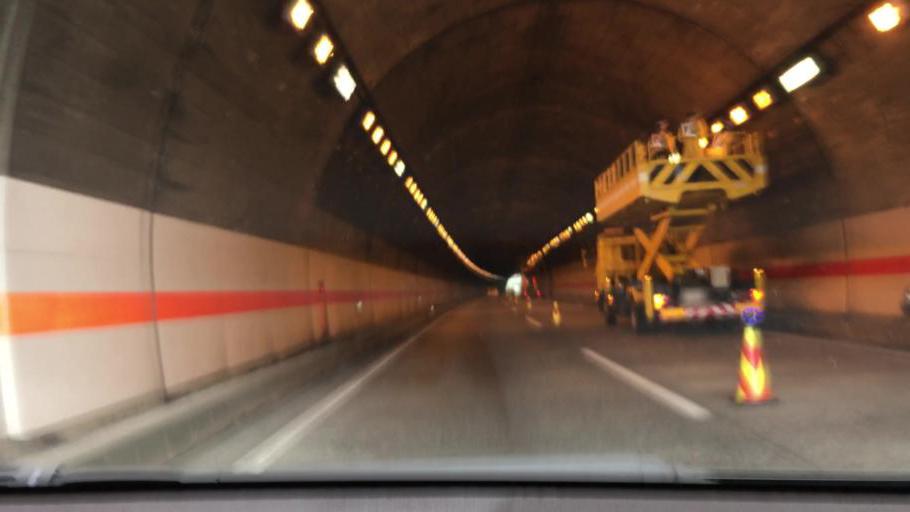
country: JP
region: Yamaguchi
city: Tokuyama
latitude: 34.0528
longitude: 131.8424
